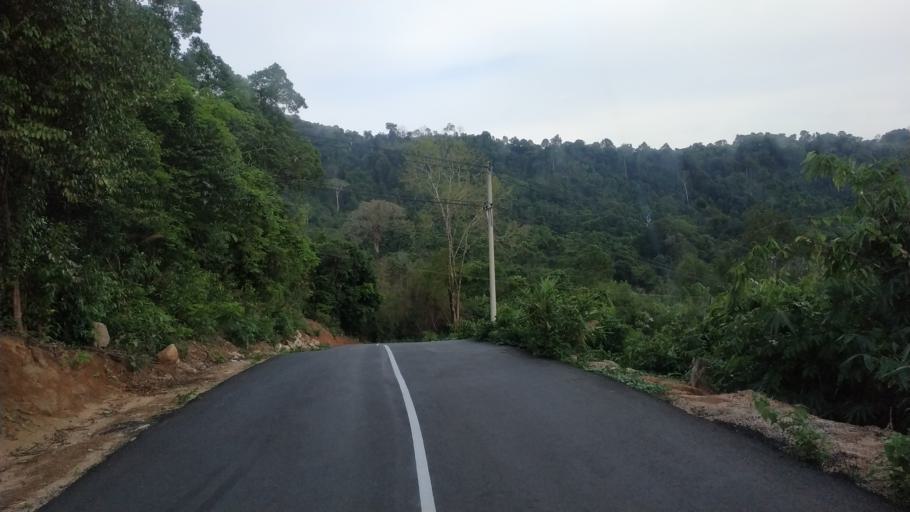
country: MM
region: Mon
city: Kyaikto
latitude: 17.4356
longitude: 97.0952
